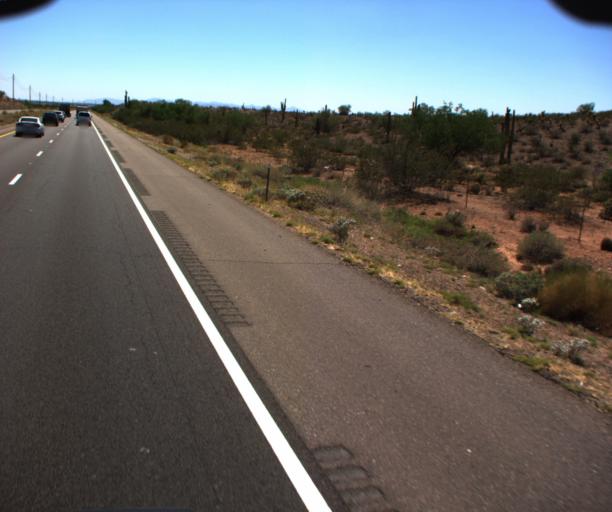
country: US
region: Arizona
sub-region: Maricopa County
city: Fountain Hills
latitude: 33.5283
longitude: -111.7340
